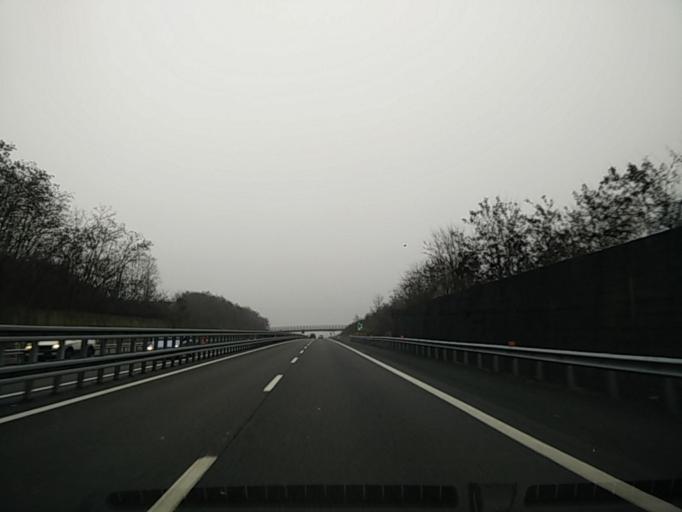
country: IT
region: Piedmont
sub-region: Provincia di Asti
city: Baldichieri d'Asti
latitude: 44.9040
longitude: 8.1075
